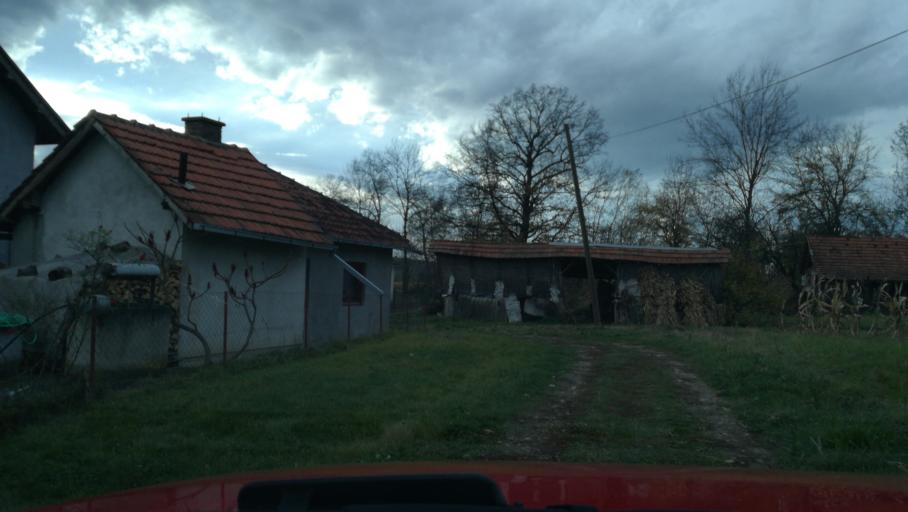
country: RS
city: Prislonica
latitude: 43.9077
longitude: 20.4313
